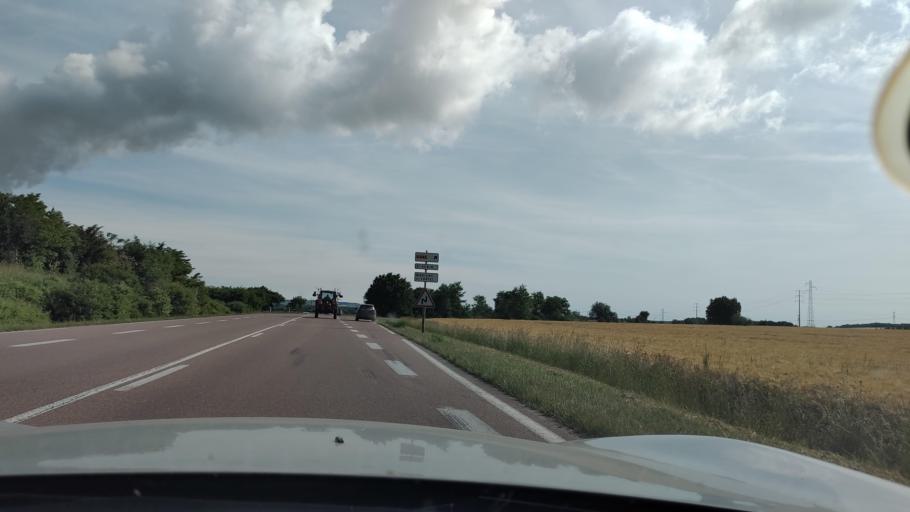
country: FR
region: Champagne-Ardenne
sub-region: Departement de l'Aube
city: Nogent-sur-Seine
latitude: 48.4885
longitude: 3.5196
